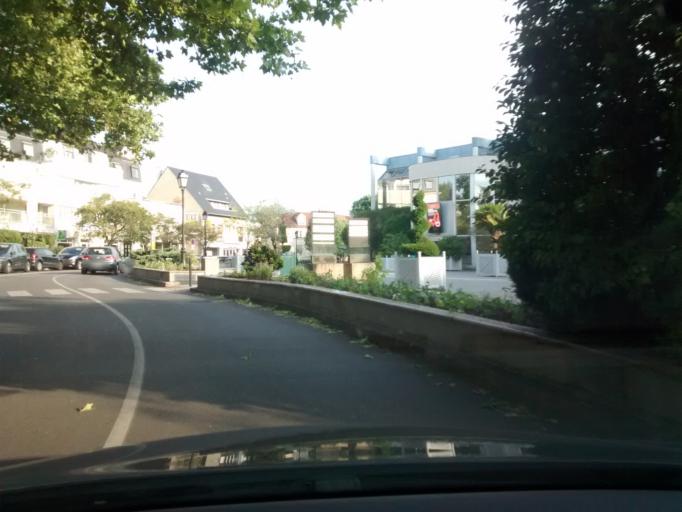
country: FR
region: Ile-de-France
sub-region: Departement des Yvelines
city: Le Chesnay
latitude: 48.8269
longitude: 2.1256
